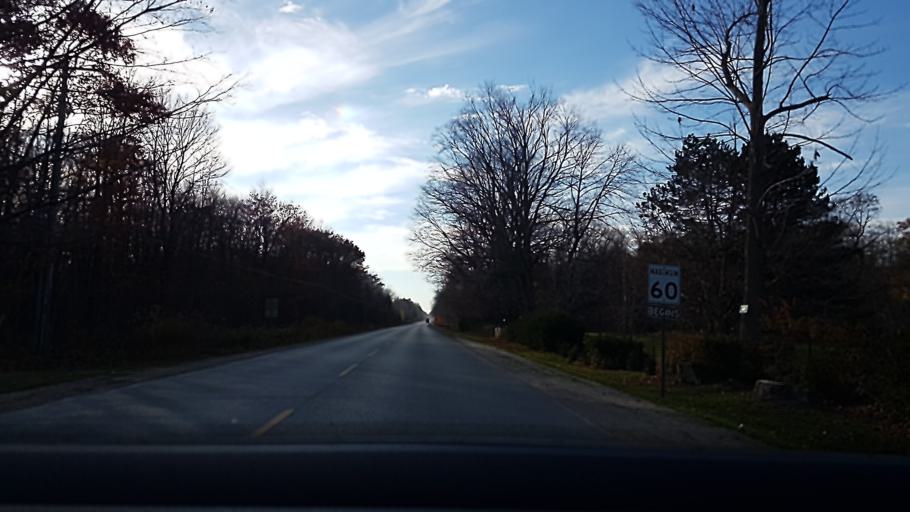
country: CA
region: Ontario
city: Barrie
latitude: 44.3978
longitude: -79.5248
